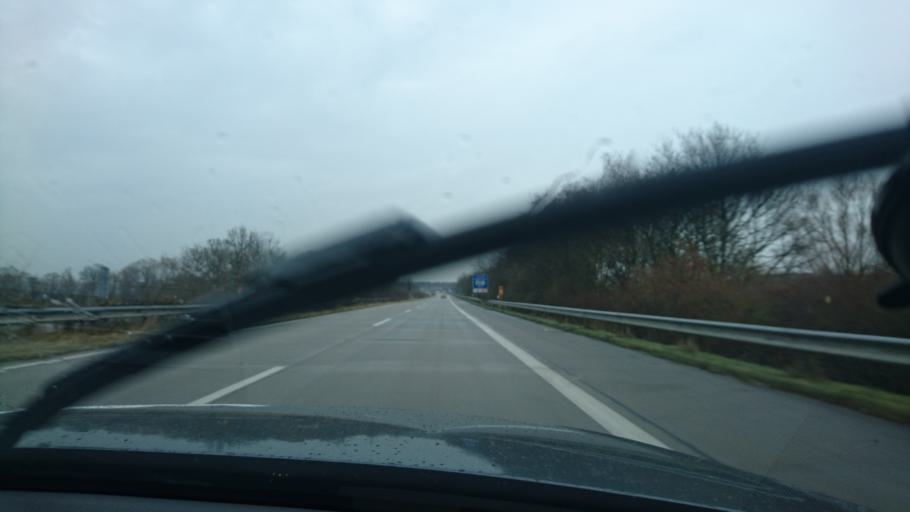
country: DE
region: Schleswig-Holstein
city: Susel
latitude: 54.0576
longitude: 10.7409
